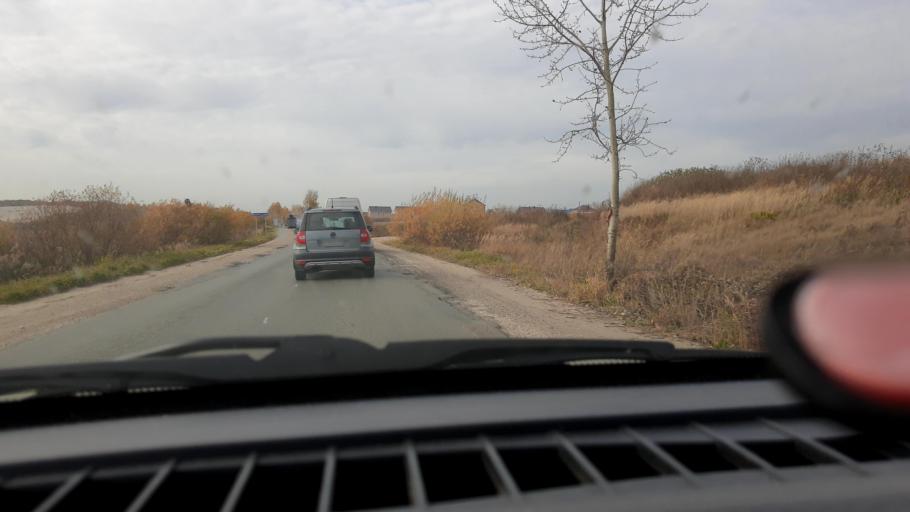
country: RU
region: Nizjnij Novgorod
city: Neklyudovo
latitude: 56.4213
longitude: 43.9557
